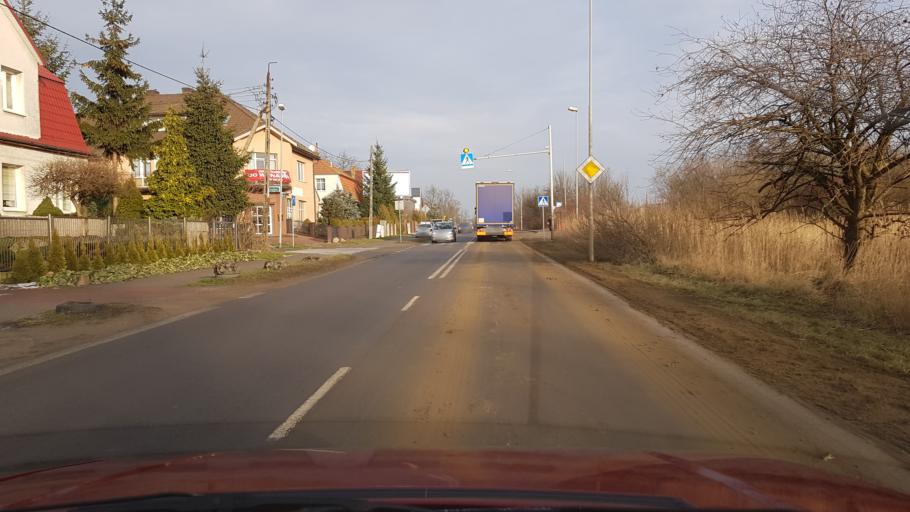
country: PL
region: West Pomeranian Voivodeship
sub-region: Powiat policki
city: Police
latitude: 53.4928
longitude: 14.5840
